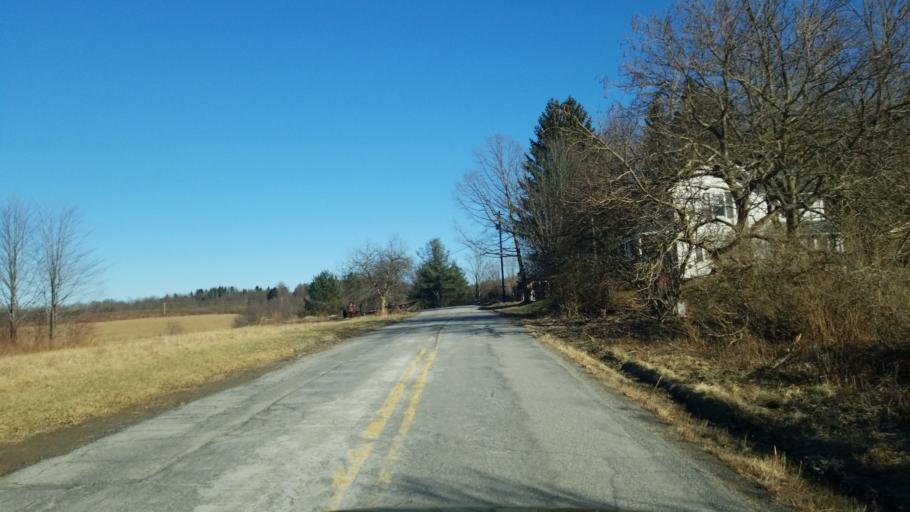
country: US
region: Pennsylvania
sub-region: Clearfield County
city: Sandy
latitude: 41.0487
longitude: -78.7527
